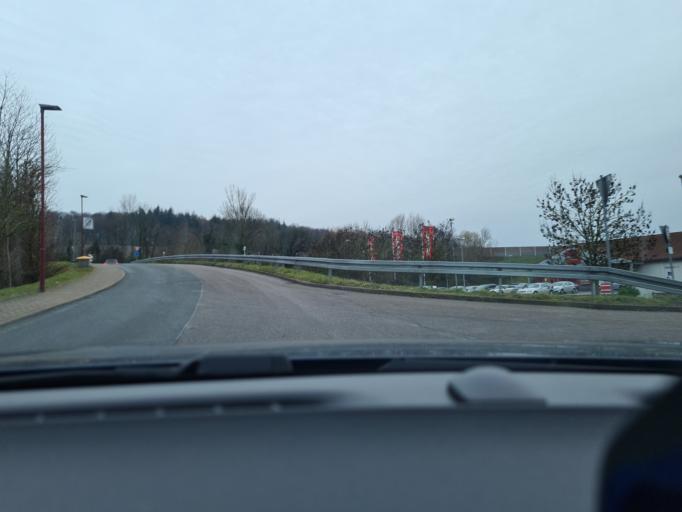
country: DE
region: Baden-Wuerttemberg
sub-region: Karlsruhe Region
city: Dielheim
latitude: 49.2821
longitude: 8.7260
